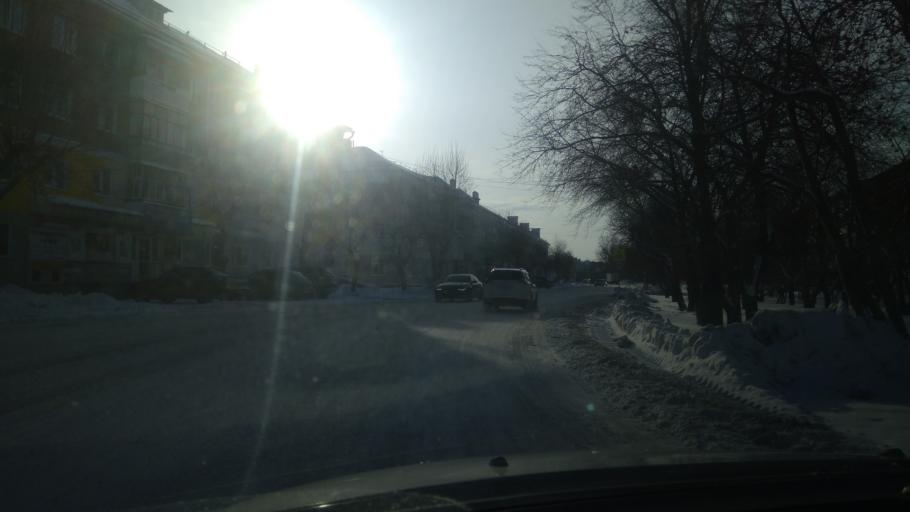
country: RU
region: Sverdlovsk
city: Sukhoy Log
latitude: 56.9082
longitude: 62.0343
